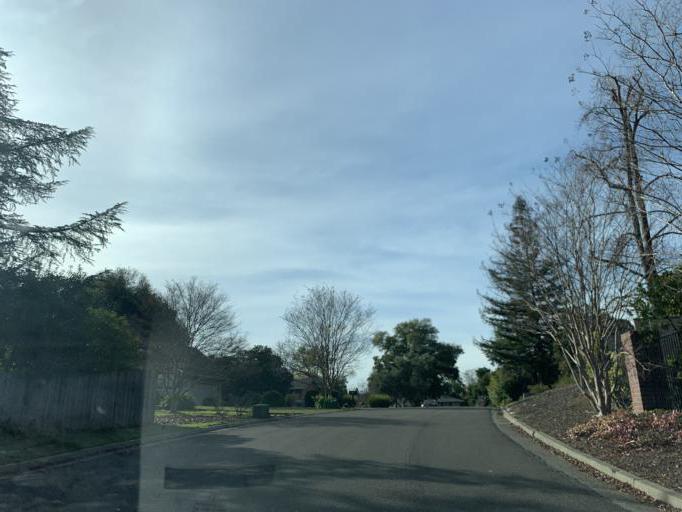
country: US
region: California
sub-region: El Dorado County
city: El Dorado Hills
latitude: 38.6559
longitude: -121.0735
